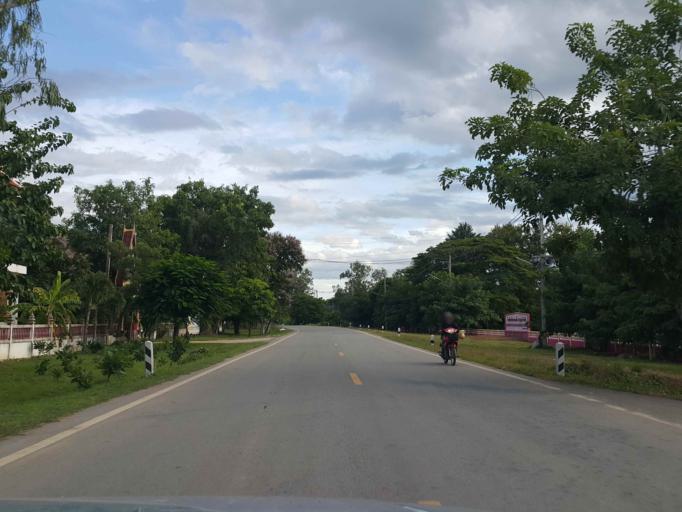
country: TH
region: Sukhothai
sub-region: Amphoe Si Satchanalai
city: Si Satchanalai
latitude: 17.5027
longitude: 99.7526
